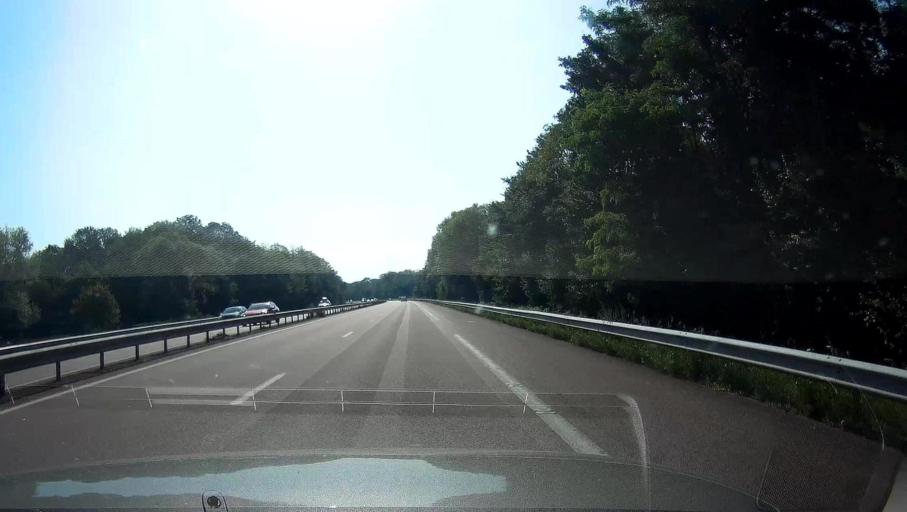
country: FR
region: Bourgogne
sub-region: Departement de la Cote-d'Or
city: Fenay
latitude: 47.2464
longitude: 5.0658
